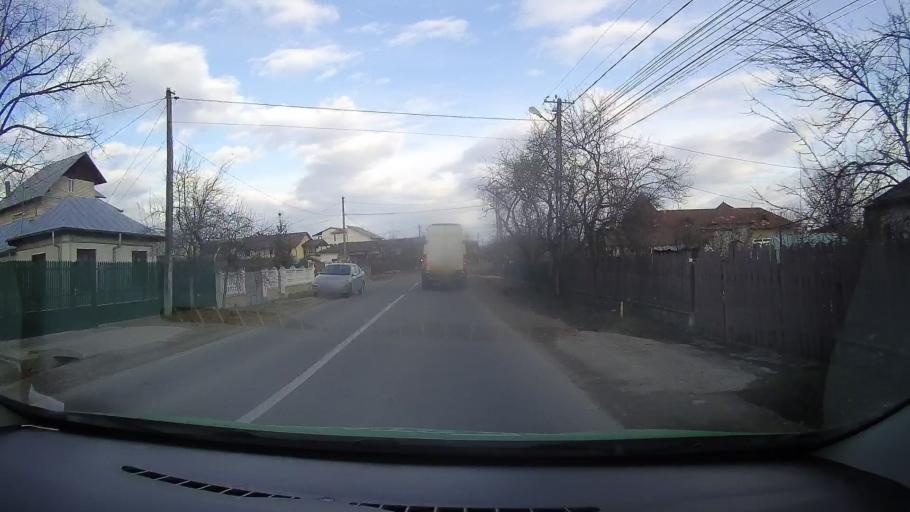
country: RO
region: Dambovita
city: Razvad
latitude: 44.9337
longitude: 25.5408
